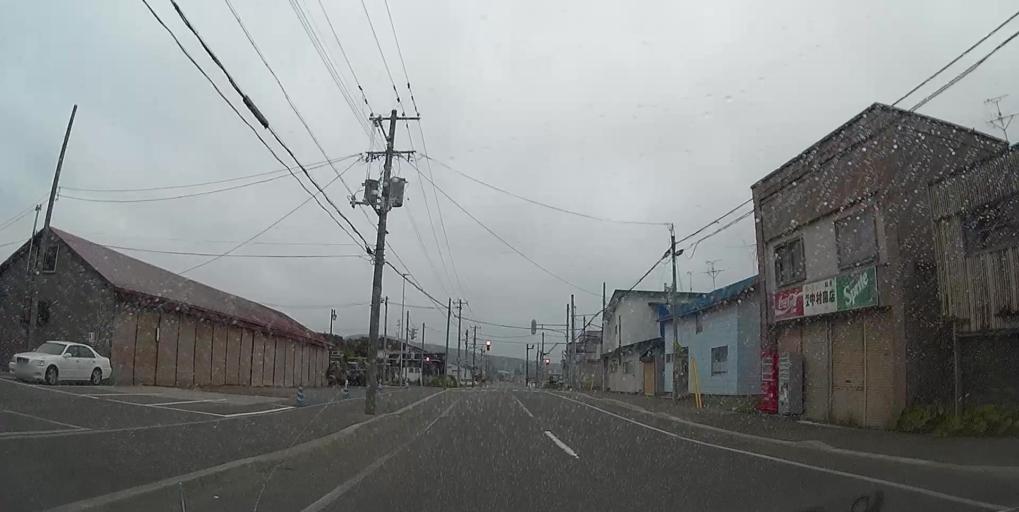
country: JP
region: Hokkaido
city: Iwanai
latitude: 42.4269
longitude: 140.0133
